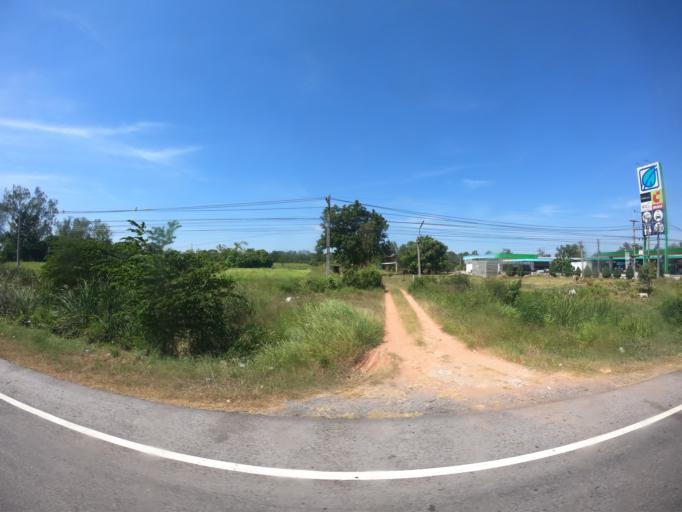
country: TH
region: Khon Kaen
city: Phon
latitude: 15.7230
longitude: 102.5924
